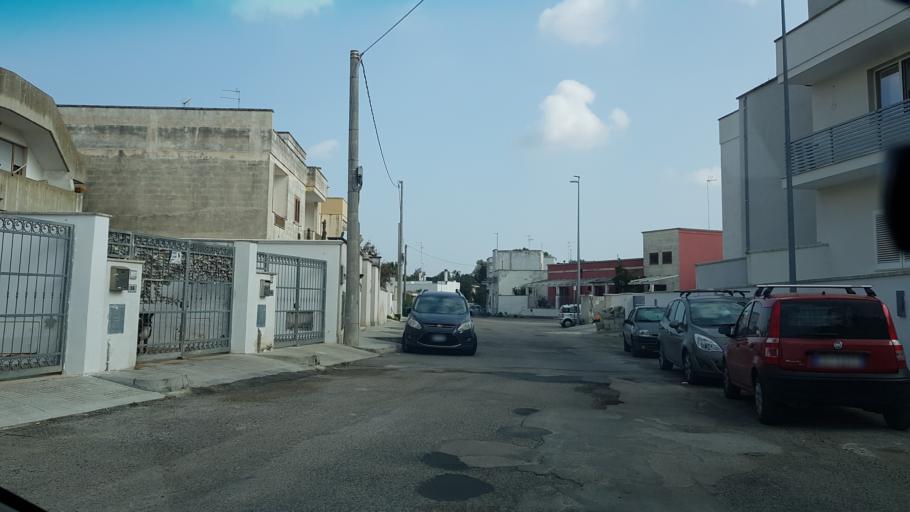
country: IT
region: Apulia
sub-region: Provincia di Lecce
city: Castromediano
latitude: 40.3252
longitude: 18.1813
